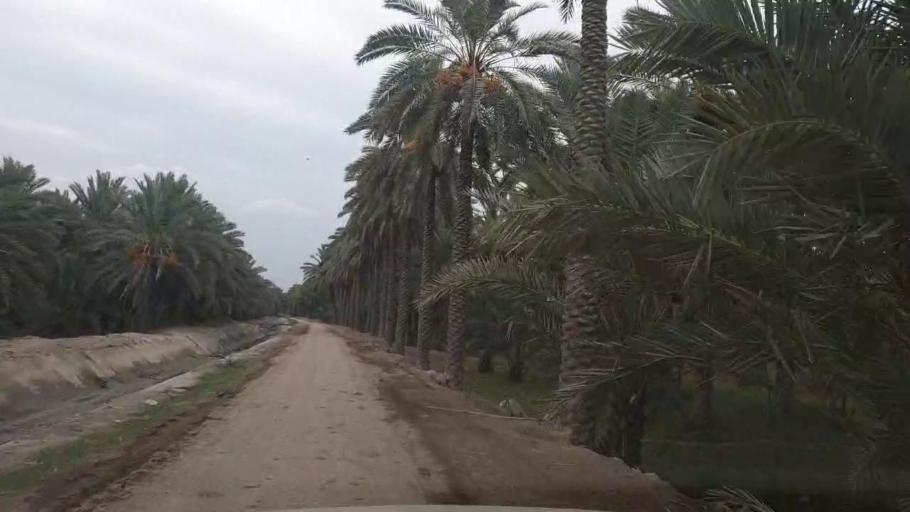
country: PK
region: Sindh
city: Khairpur
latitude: 27.5974
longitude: 68.8008
